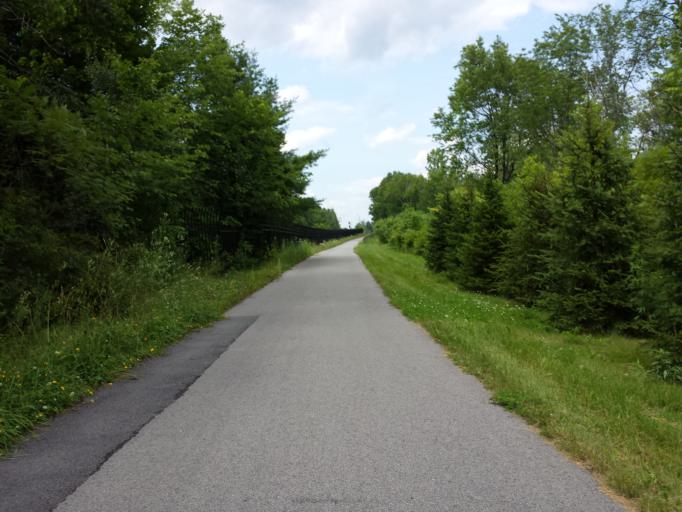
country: US
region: New York
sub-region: Saratoga County
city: Ballston Spa
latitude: 42.9934
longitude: -73.8410
